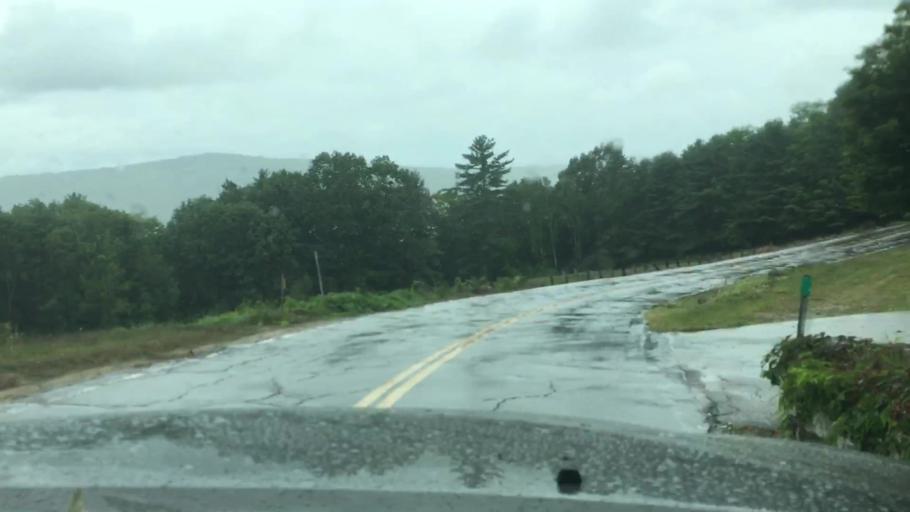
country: US
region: New Hampshire
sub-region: Belknap County
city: Meredith
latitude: 43.6725
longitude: -71.5280
